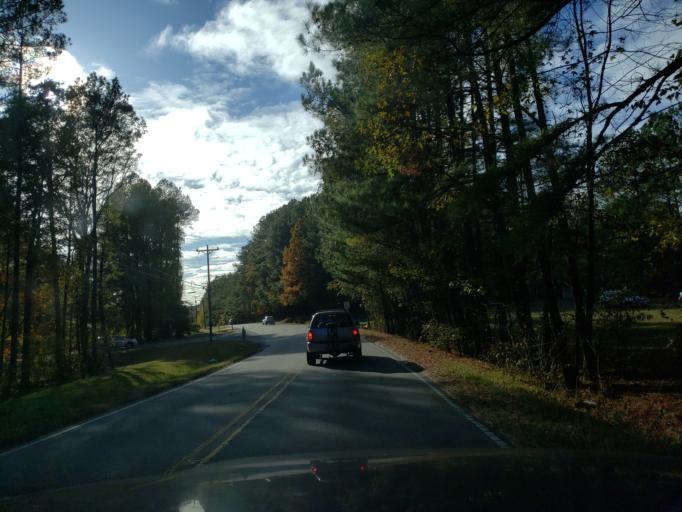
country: US
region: North Carolina
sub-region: Durham County
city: Durham
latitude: 35.9343
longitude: -78.9126
